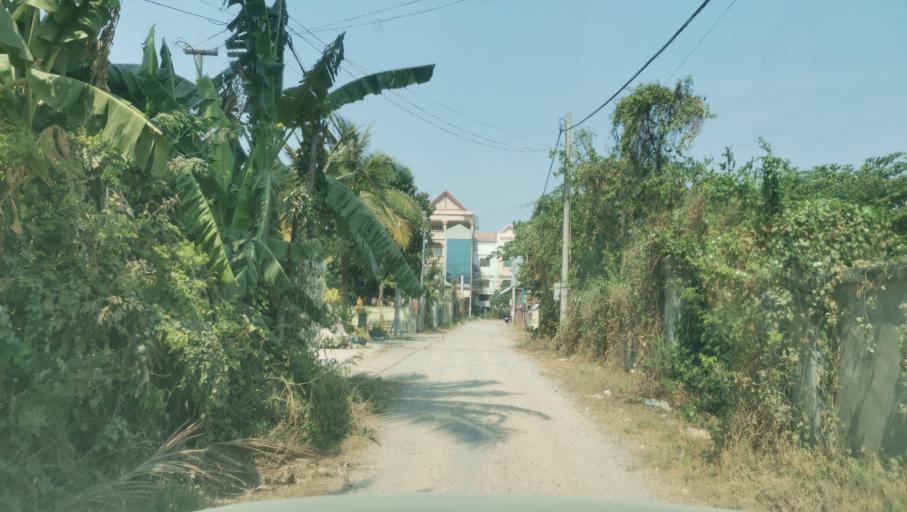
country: KH
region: Battambang
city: Battambang
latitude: 13.0898
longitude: 103.1961
